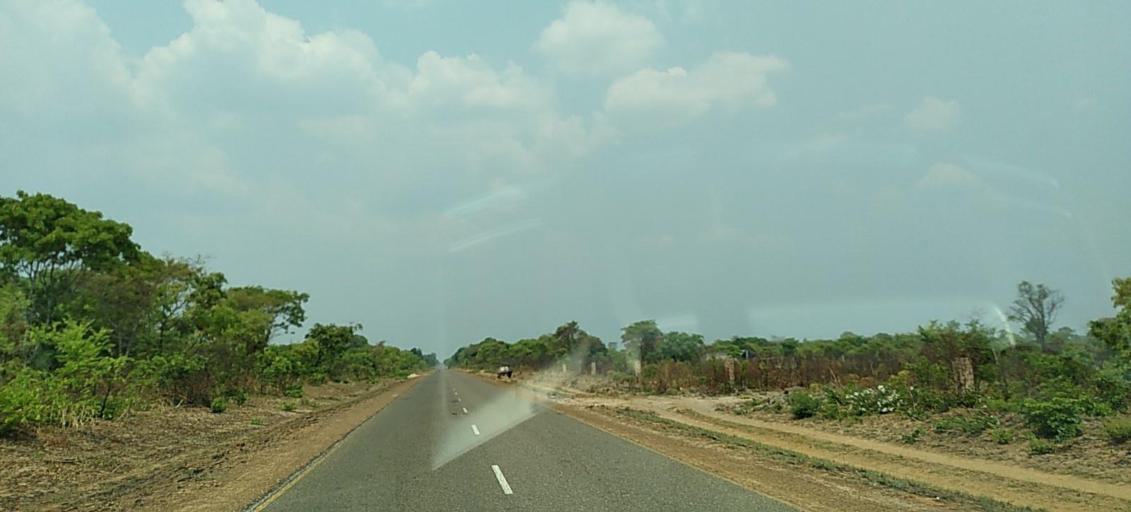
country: ZM
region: North-Western
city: Zambezi
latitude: -13.5534
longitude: 23.1516
